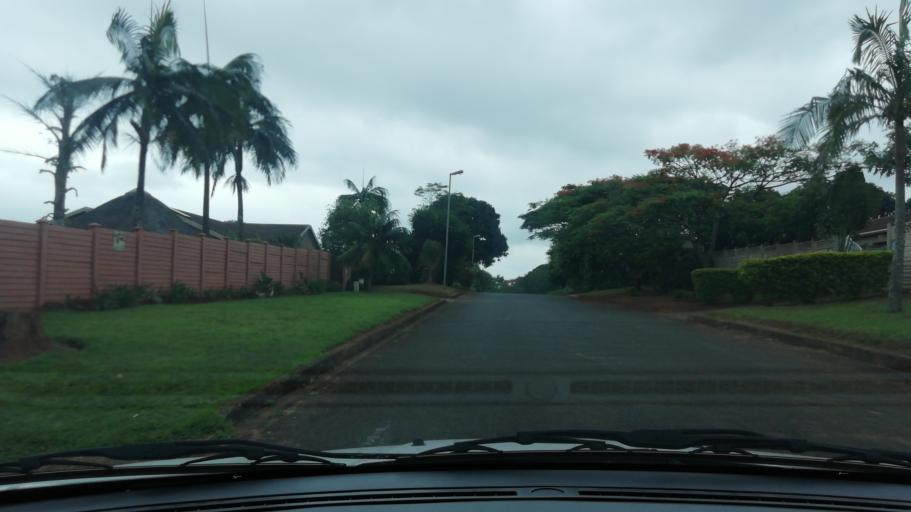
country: ZA
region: KwaZulu-Natal
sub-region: uThungulu District Municipality
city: Empangeni
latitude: -28.7659
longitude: 31.9007
